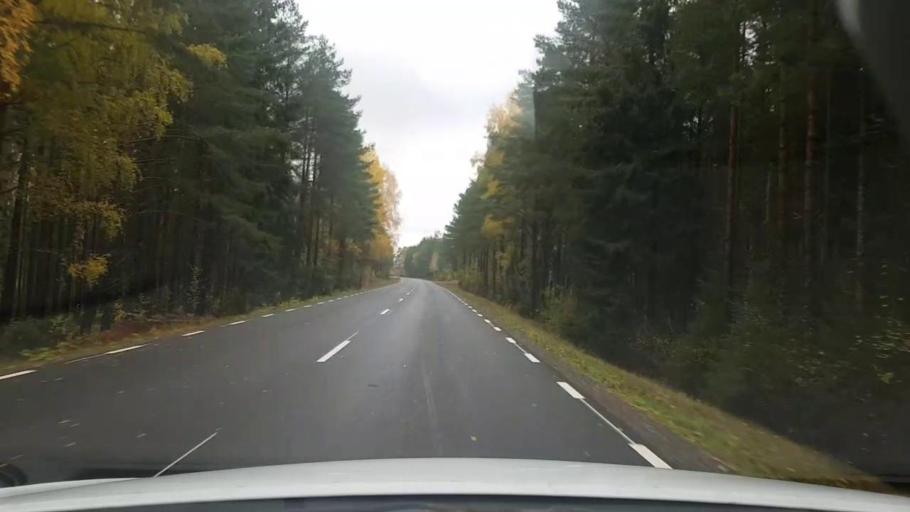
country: SE
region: OErebro
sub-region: Laxa Kommun
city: Laxa
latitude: 58.8498
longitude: 14.5486
